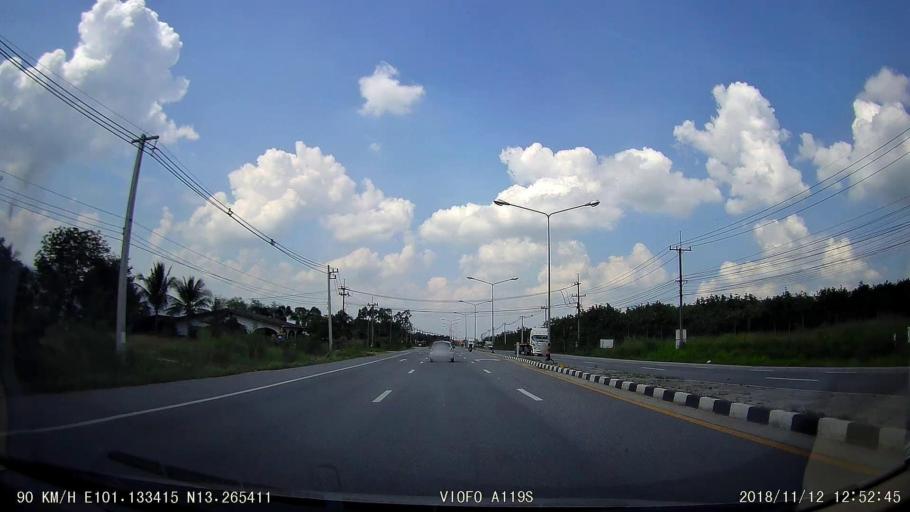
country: TH
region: Chon Buri
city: Ban Bueng
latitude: 13.2657
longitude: 101.1332
